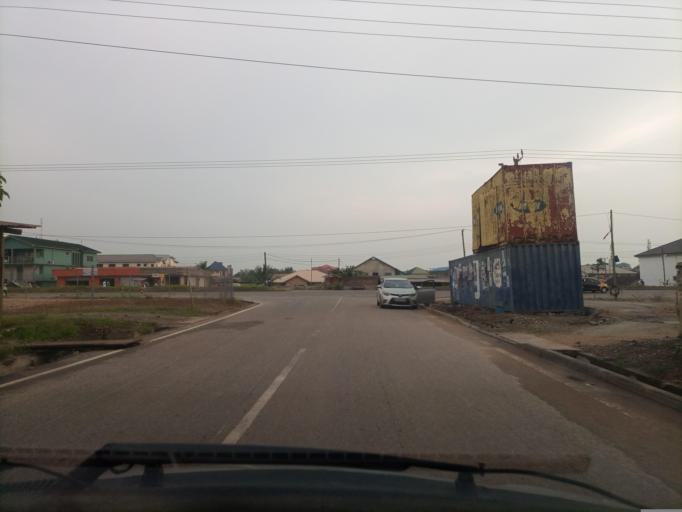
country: GH
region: Western
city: Takoradi
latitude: 4.9283
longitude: -1.7822
